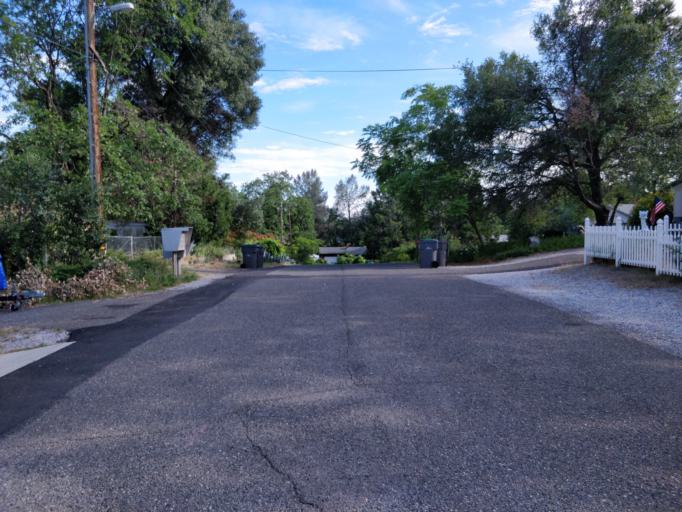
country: US
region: California
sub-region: Shasta County
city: Shasta Lake
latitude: 40.6849
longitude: -122.3696
